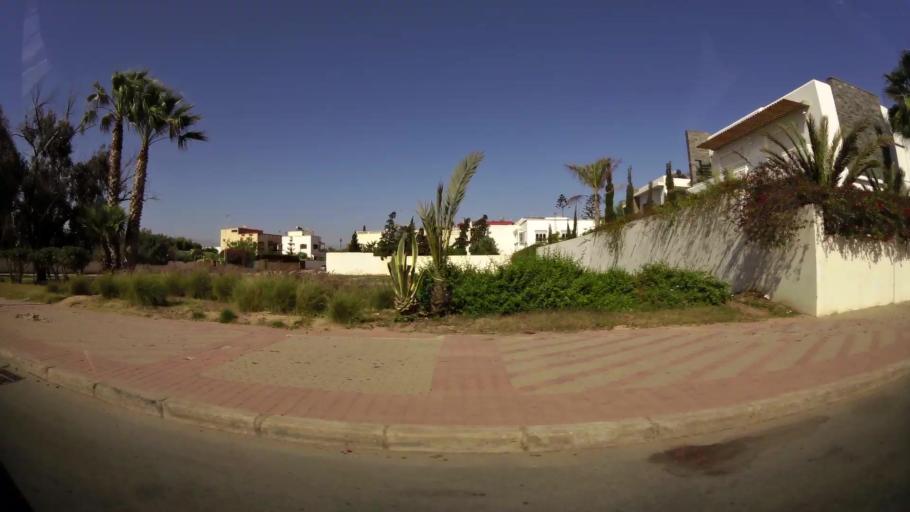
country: MA
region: Oued ed Dahab-Lagouira
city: Dakhla
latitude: 30.3920
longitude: -9.5773
